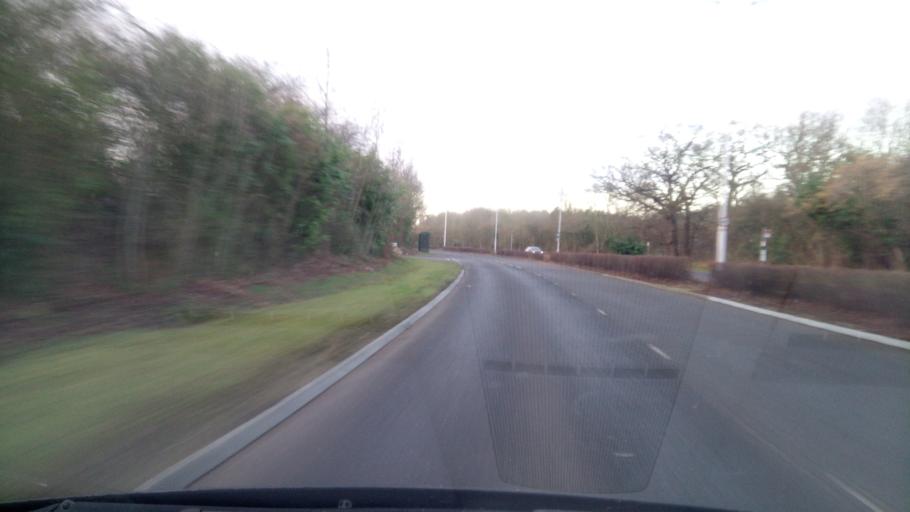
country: GB
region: England
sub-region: Peterborough
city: Marholm
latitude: 52.5751
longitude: -0.2954
